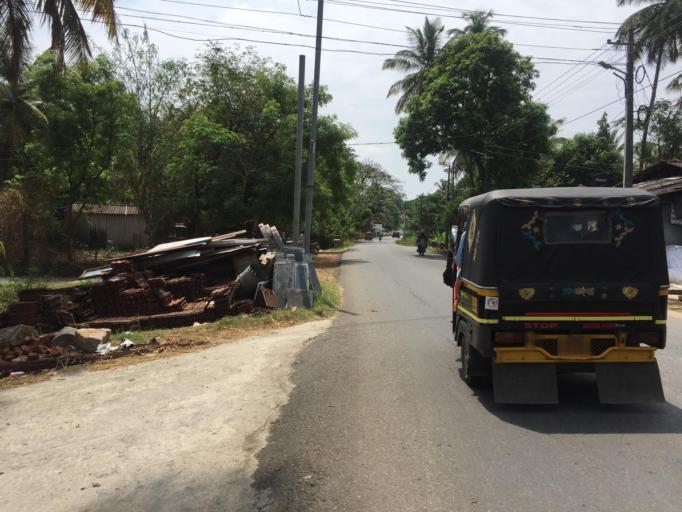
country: IN
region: Kerala
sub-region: Palakkad district
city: Chittur
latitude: 10.6813
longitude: 76.7146
